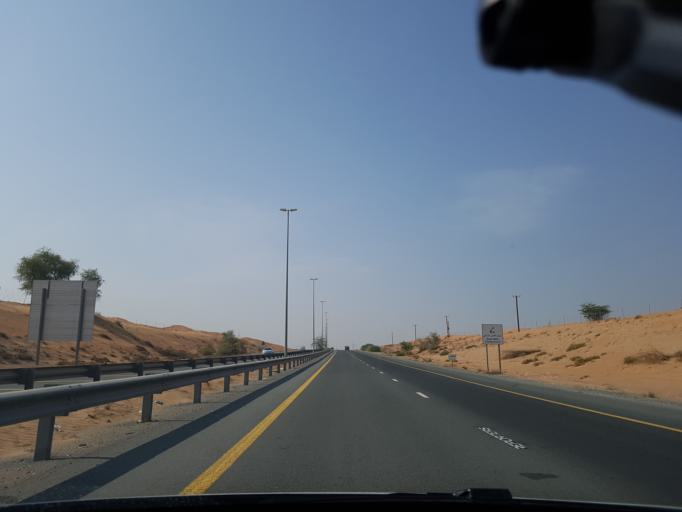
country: AE
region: Umm al Qaywayn
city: Umm al Qaywayn
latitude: 25.5170
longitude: 55.7434
